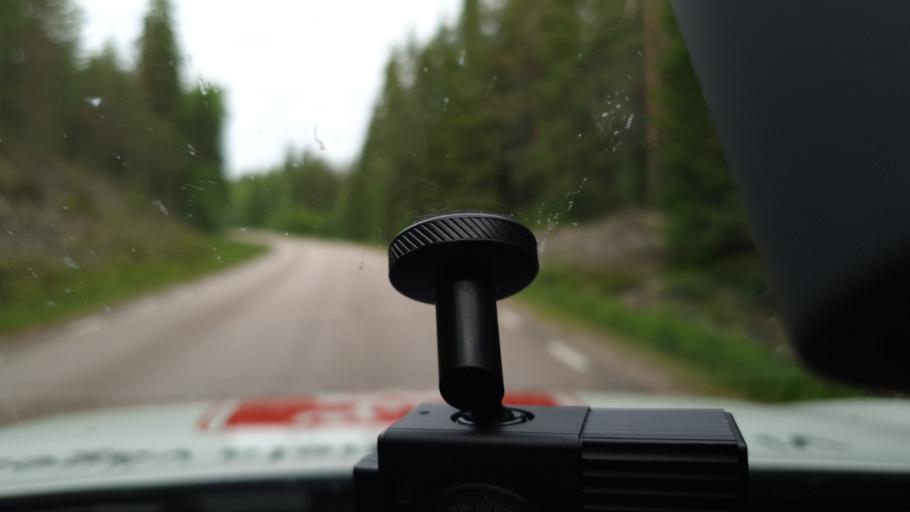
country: SE
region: Vaermland
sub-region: Torsby Kommun
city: Torsby
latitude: 60.1106
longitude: 12.9145
